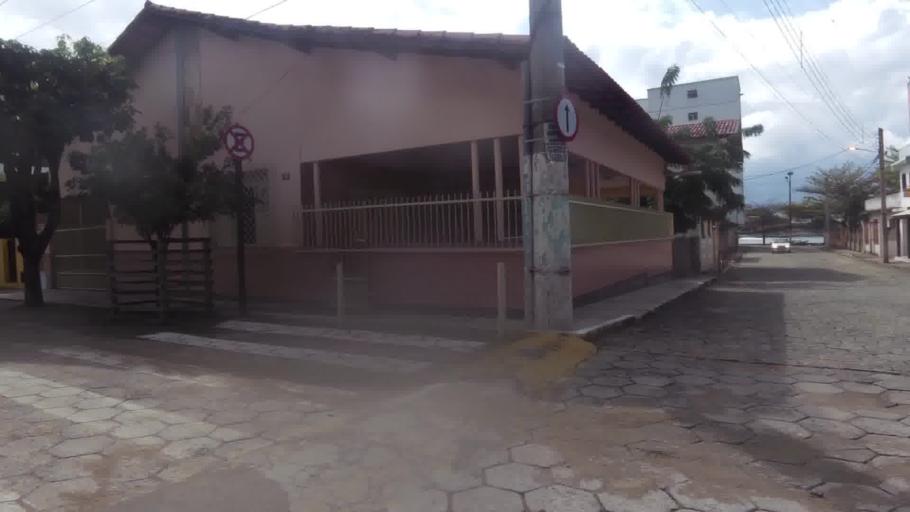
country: BR
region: Espirito Santo
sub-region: Piuma
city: Piuma
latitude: -20.8325
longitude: -40.6950
